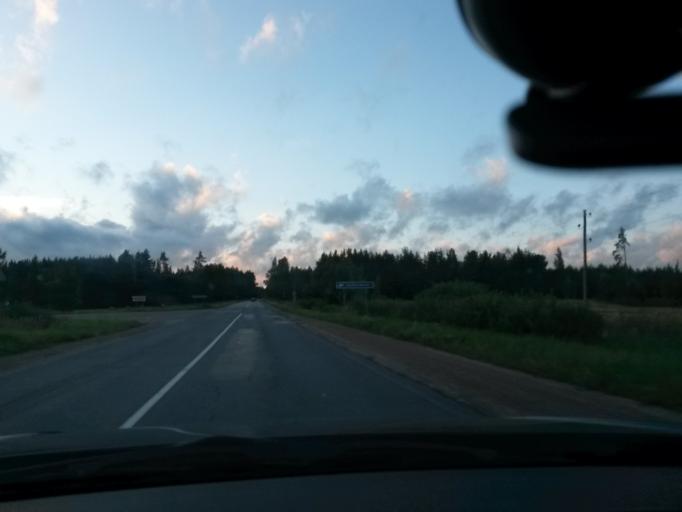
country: LV
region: Jekabpils Rajons
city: Jekabpils
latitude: 56.6922
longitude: 25.9833
